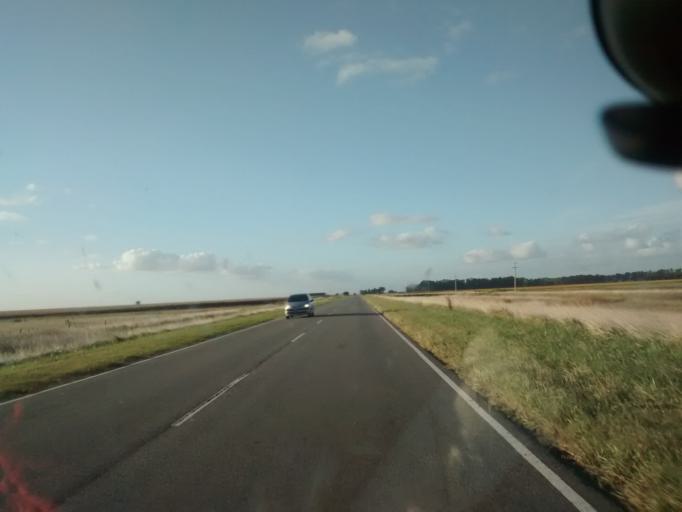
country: AR
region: Buenos Aires
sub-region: Partido de General Belgrano
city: General Belgrano
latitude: -36.0517
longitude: -58.6250
